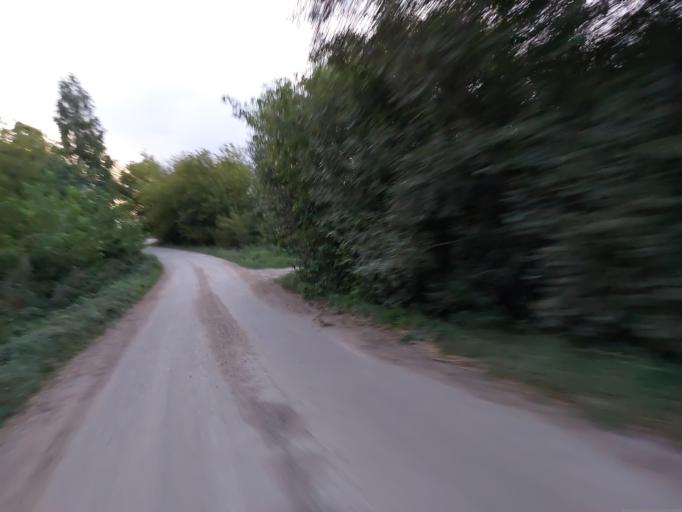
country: RU
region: Lipetsk
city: Dolgorukovo
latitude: 52.3791
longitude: 38.0471
